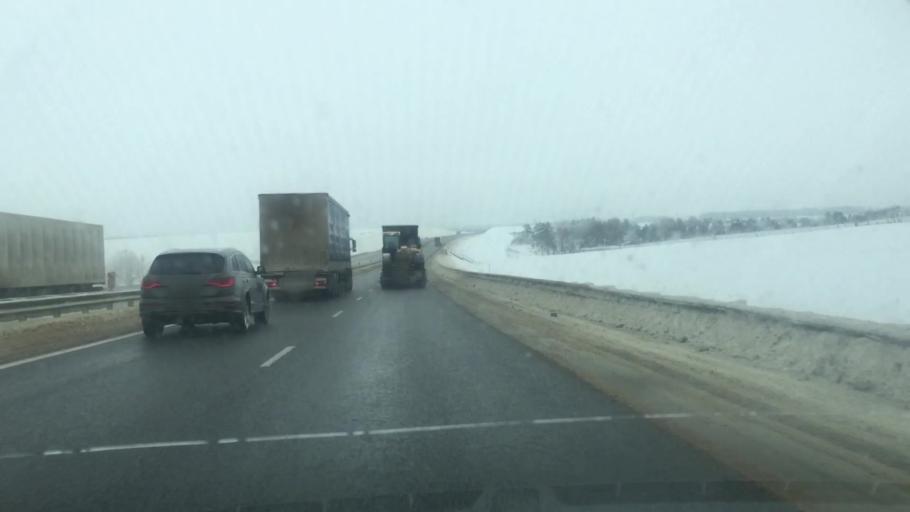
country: RU
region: Lipetsk
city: Stanovoye
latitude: 52.7903
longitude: 38.3587
